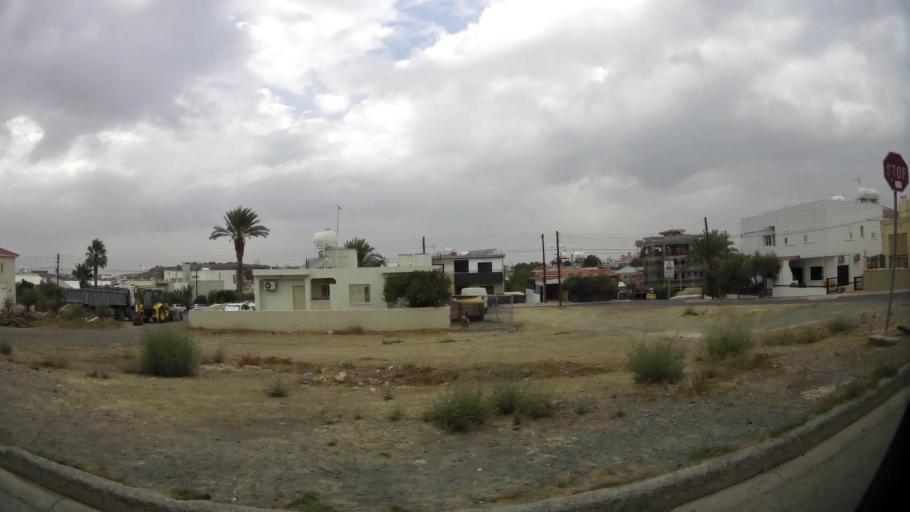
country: CY
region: Lefkosia
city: Geri
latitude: 35.1191
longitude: 33.3816
